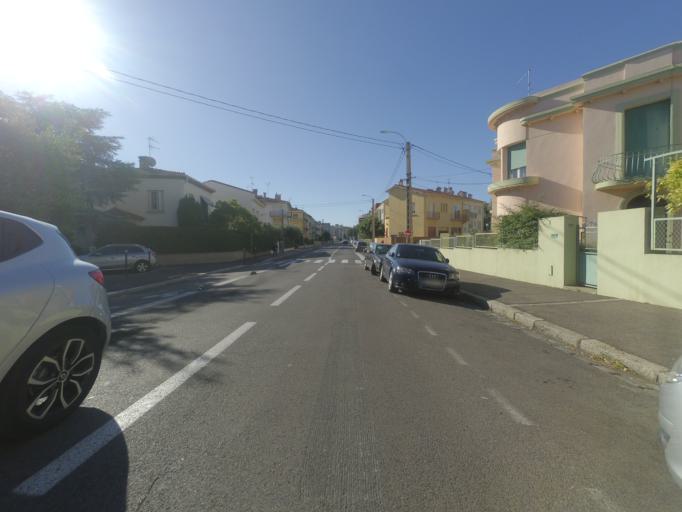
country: FR
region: Languedoc-Roussillon
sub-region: Departement des Pyrenees-Orientales
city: Perpignan
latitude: 42.6924
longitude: 2.9006
